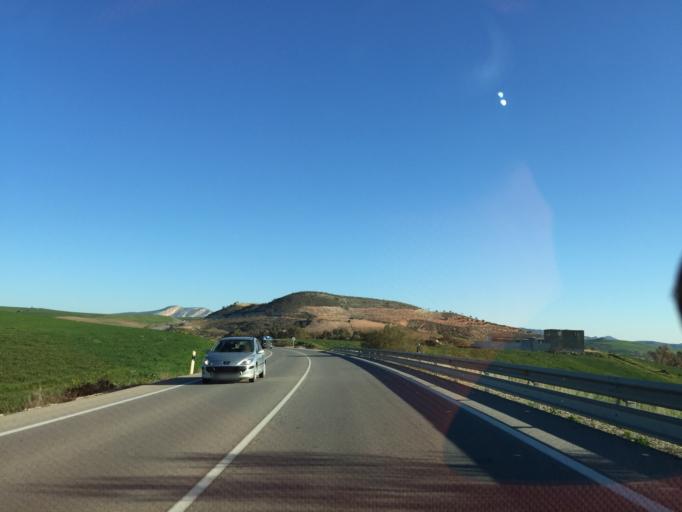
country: ES
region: Andalusia
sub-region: Provincia de Malaga
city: Ardales
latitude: 36.9022
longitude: -4.8405
